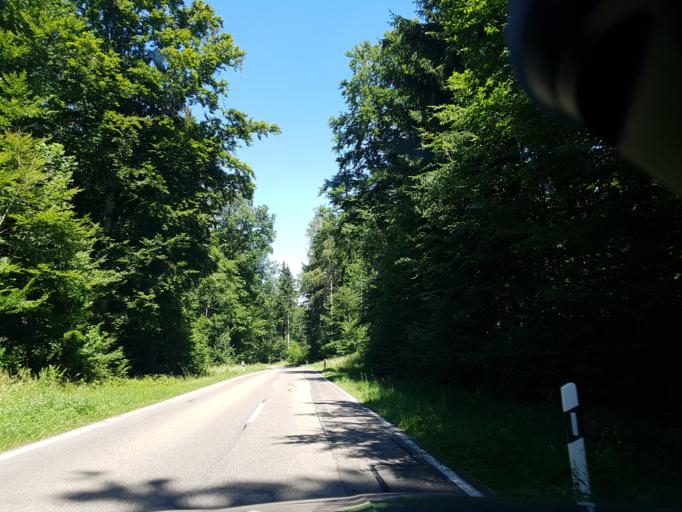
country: DE
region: Baden-Wuerttemberg
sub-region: Tuebingen Region
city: Blaubeuren
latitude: 48.4222
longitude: 9.8526
